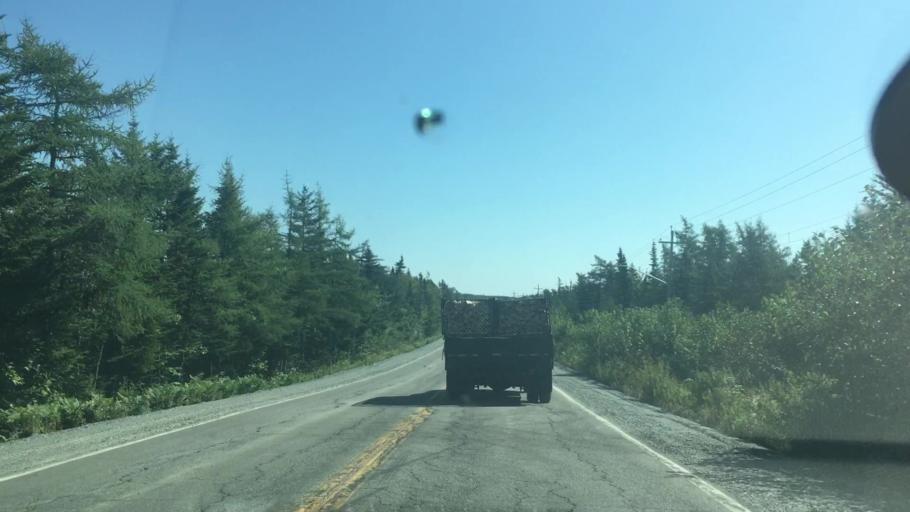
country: CA
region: Nova Scotia
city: New Glasgow
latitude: 44.9043
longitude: -62.4649
